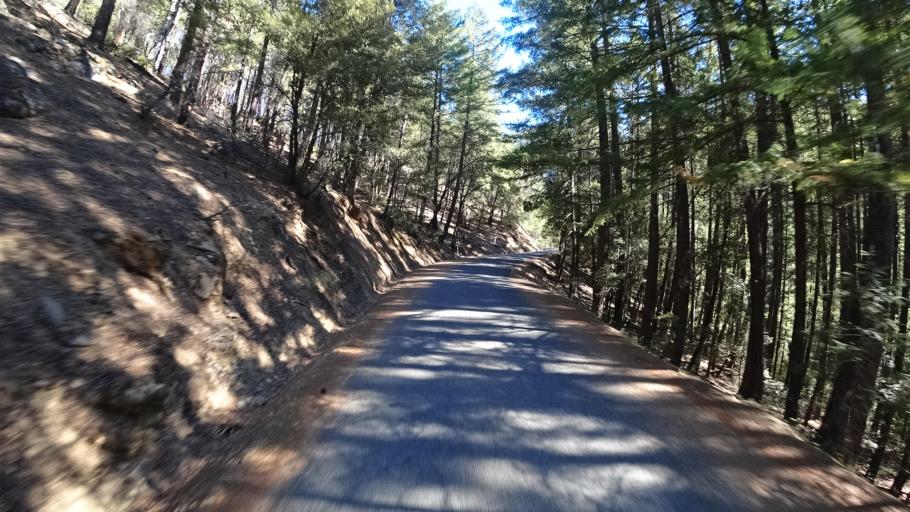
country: US
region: California
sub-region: Siskiyou County
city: Happy Camp
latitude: 41.2942
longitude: -123.2374
